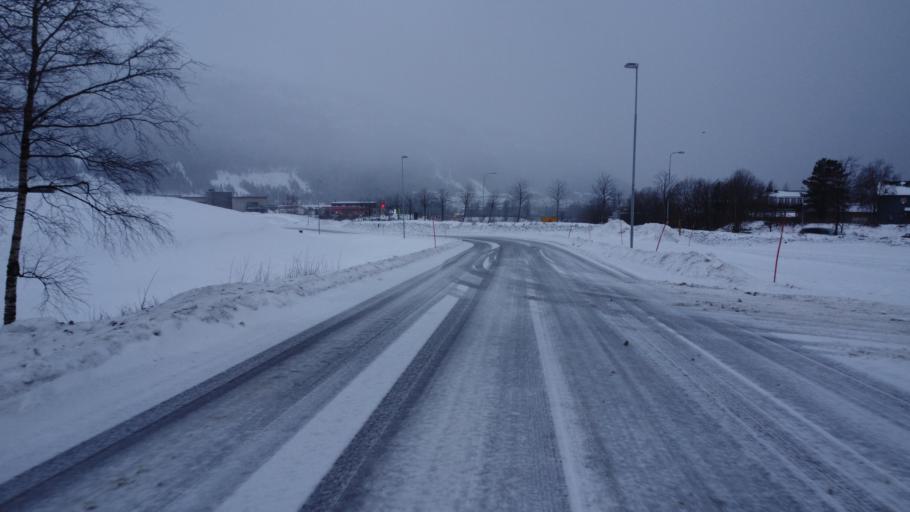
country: NO
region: Nordland
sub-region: Rana
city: Mo i Rana
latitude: 66.3102
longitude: 14.1555
